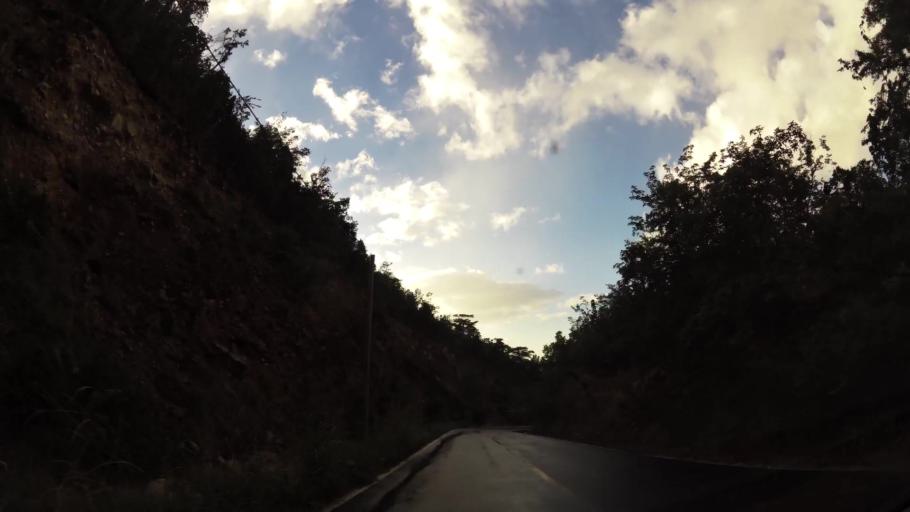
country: DM
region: Saint Peter
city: Colihaut
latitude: 15.5281
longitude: -61.4672
